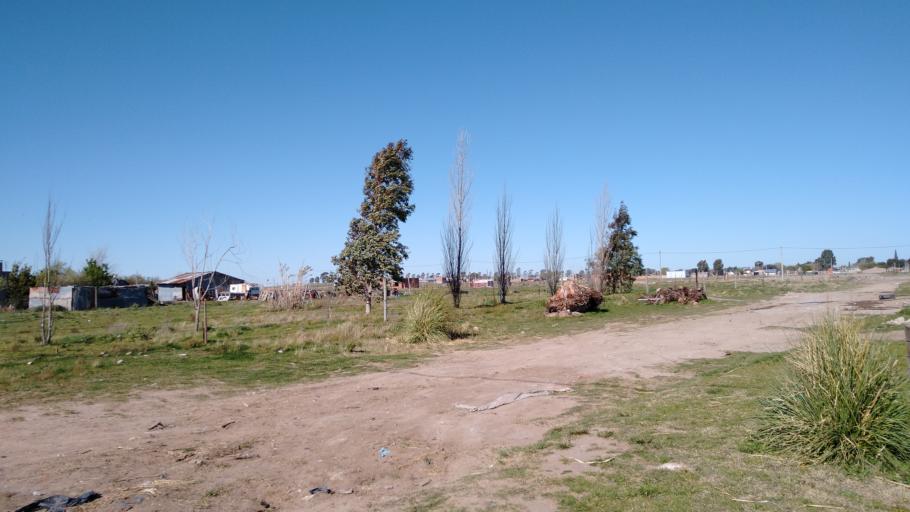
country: AR
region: Buenos Aires
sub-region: Partido de Bahia Blanca
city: Bahia Blanca
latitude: -38.7103
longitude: -62.1964
